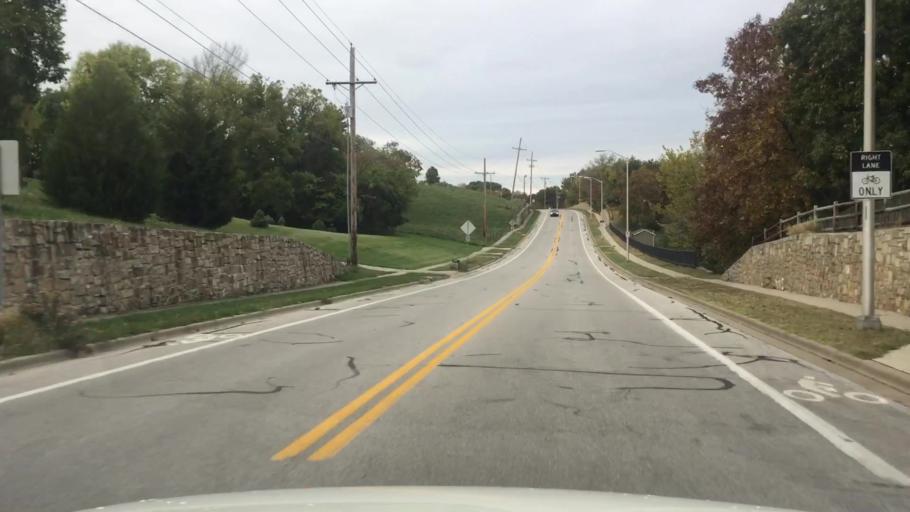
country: US
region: Kansas
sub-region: Johnson County
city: Shawnee
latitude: 39.0366
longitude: -94.7461
